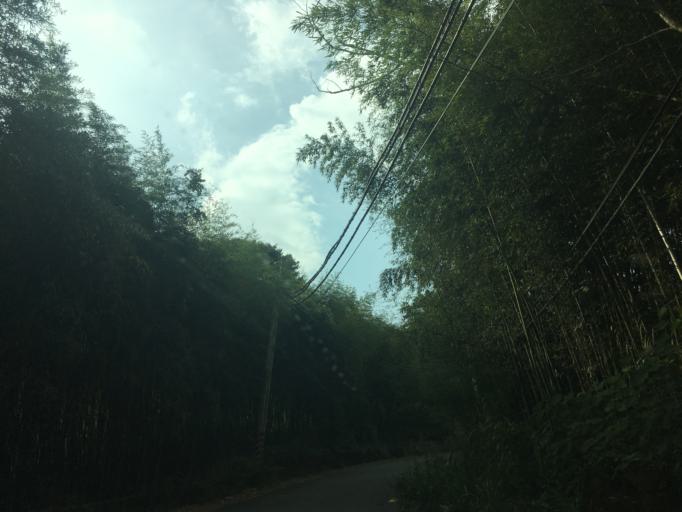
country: TW
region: Taiwan
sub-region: Miaoli
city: Miaoli
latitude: 24.3982
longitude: 120.9778
